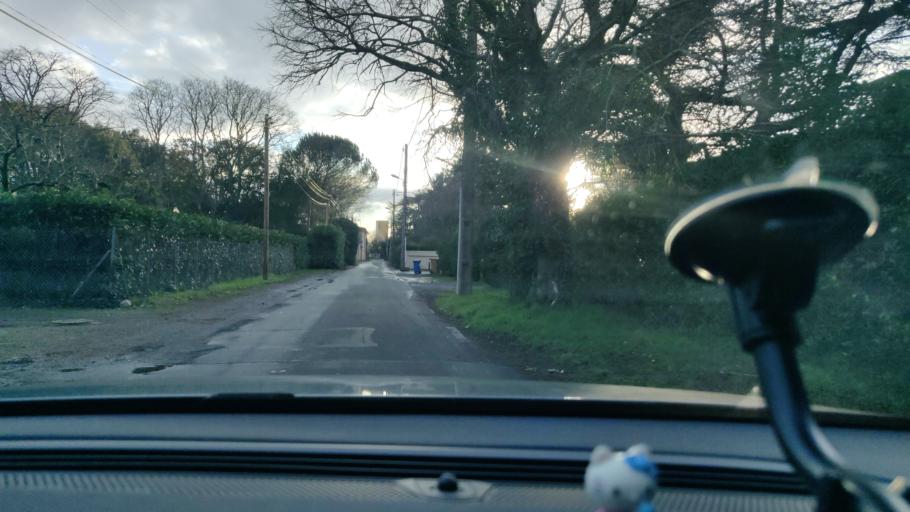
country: FR
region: Midi-Pyrenees
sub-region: Departement de la Haute-Garonne
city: Cugnaux
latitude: 43.5532
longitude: 1.3800
